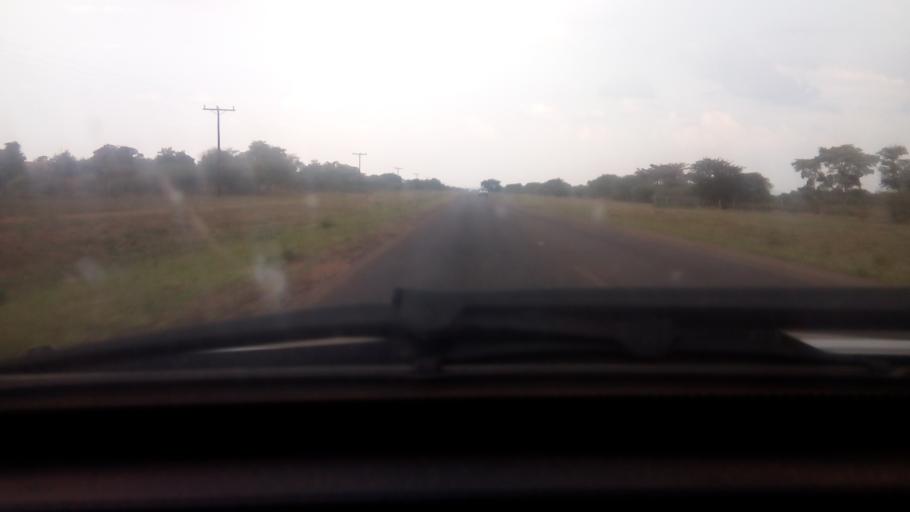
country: BW
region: Kweneng
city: Metsemotlhaba
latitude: -24.4853
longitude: 25.7363
